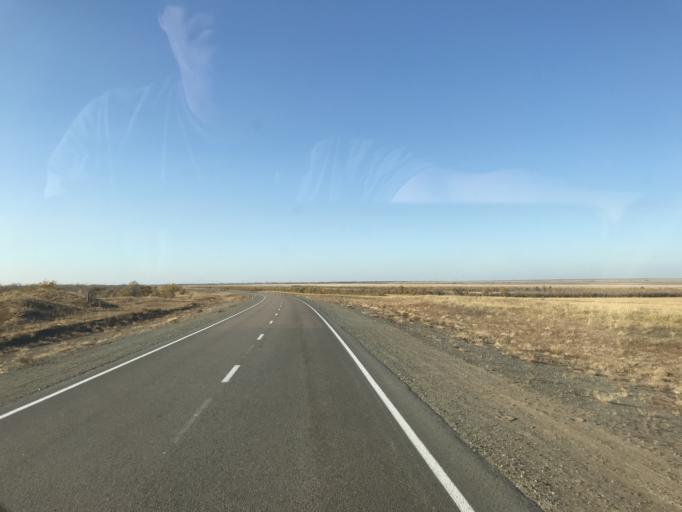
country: KZ
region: Pavlodar
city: Koktobe
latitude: 51.8576
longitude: 77.4500
